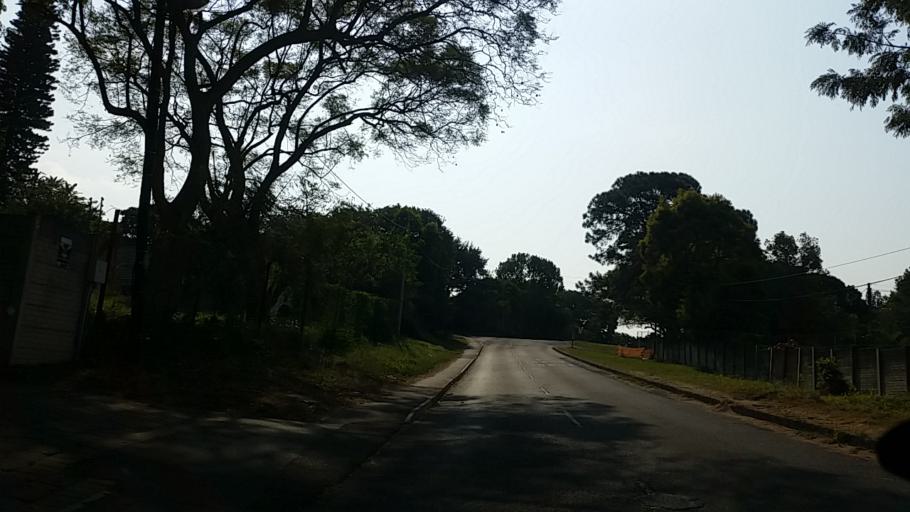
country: ZA
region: KwaZulu-Natal
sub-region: eThekwini Metropolitan Municipality
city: Berea
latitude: -29.8413
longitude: 30.9404
